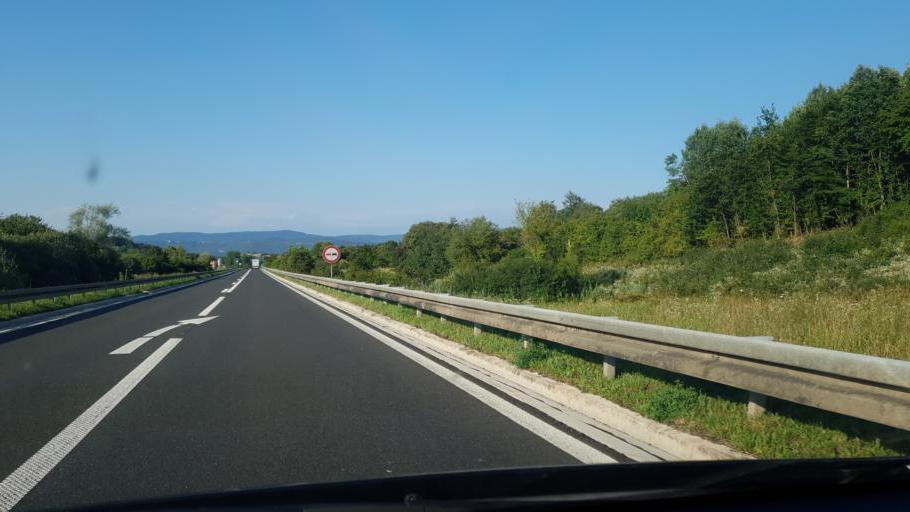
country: HR
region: Istarska
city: Pazin
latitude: 45.2979
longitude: 14.0469
